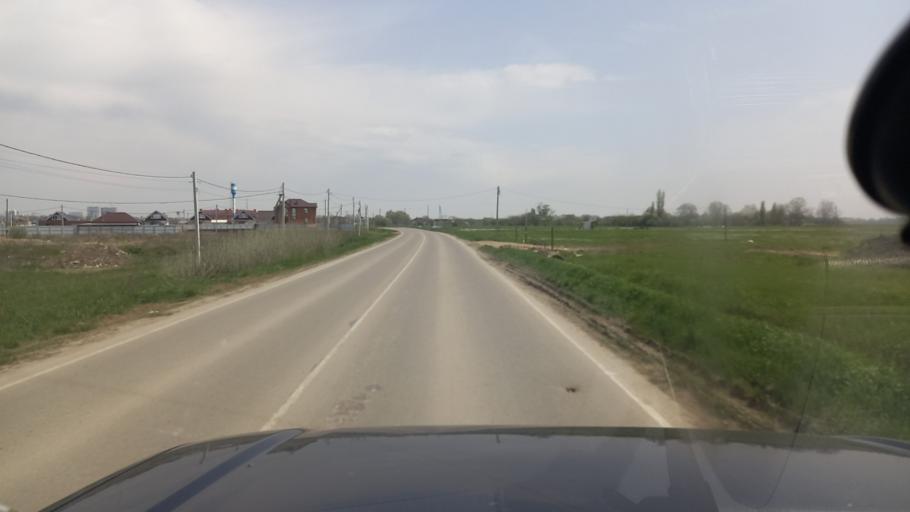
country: RU
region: Adygeya
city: Yablonovskiy
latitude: 44.9869
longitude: 38.9856
